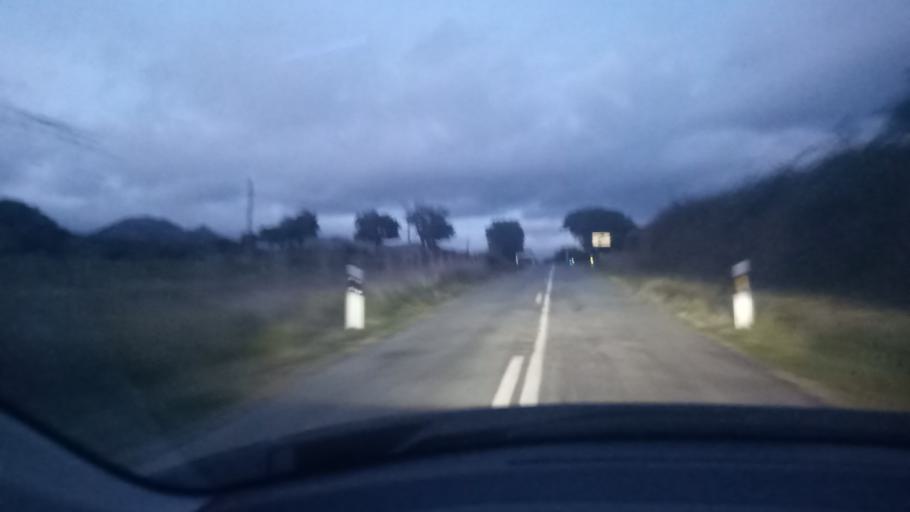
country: ES
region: Madrid
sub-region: Provincia de Madrid
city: Colmenar del Arroyo
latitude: 40.4356
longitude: -4.2442
